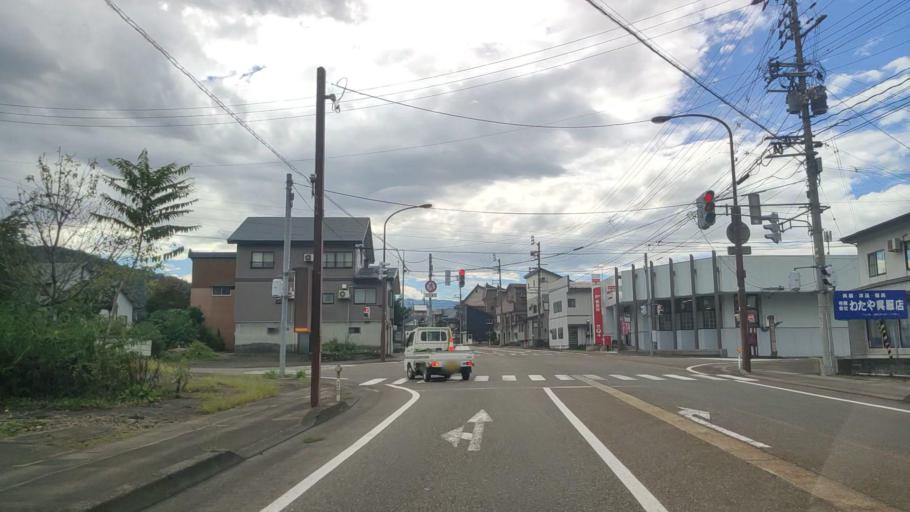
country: JP
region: Niigata
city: Arai
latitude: 36.9876
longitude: 138.2716
